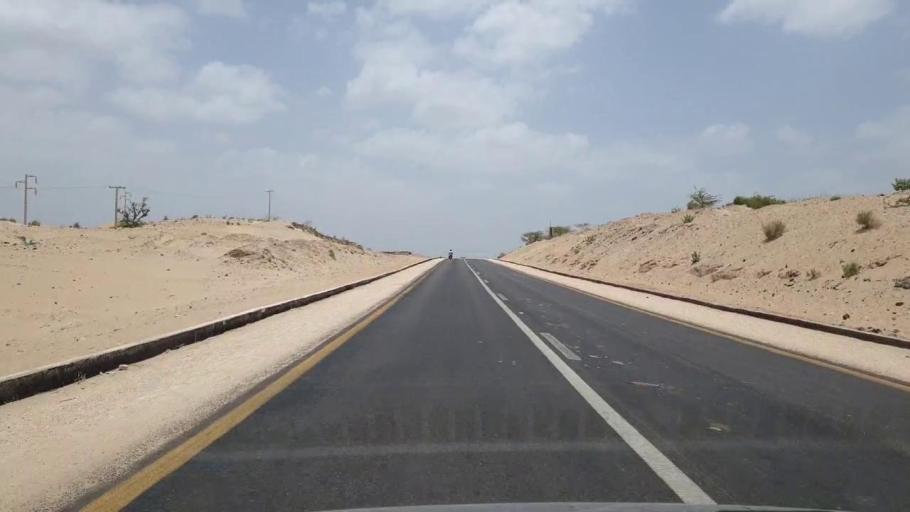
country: PK
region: Sindh
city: Naukot
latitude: 24.8391
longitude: 69.4609
